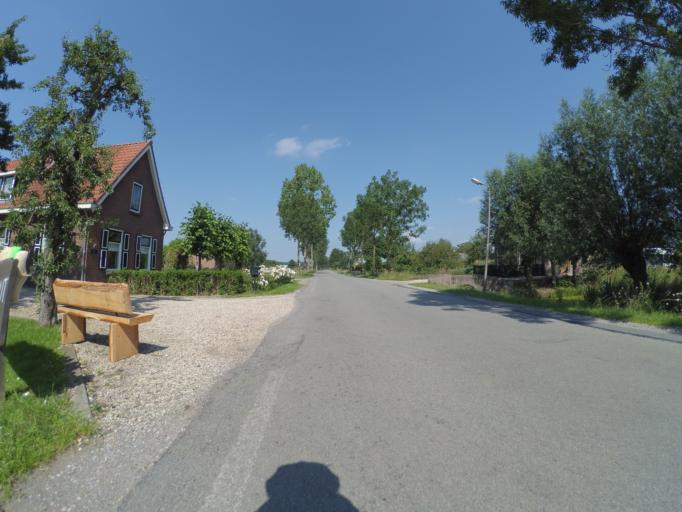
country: NL
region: South Holland
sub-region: Gemeente Leerdam
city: Leerdam
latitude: 51.9315
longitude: 5.1219
